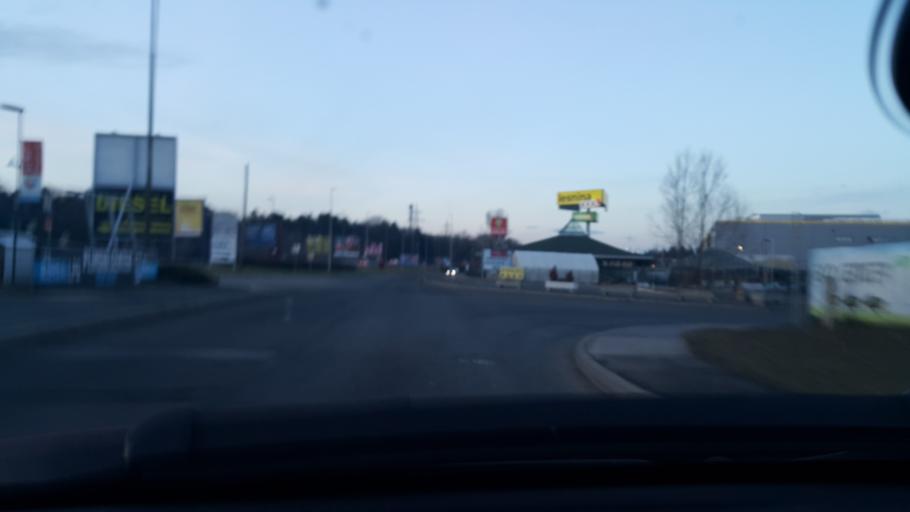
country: SI
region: Maribor
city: Razvanje
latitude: 46.5291
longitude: 15.6469
